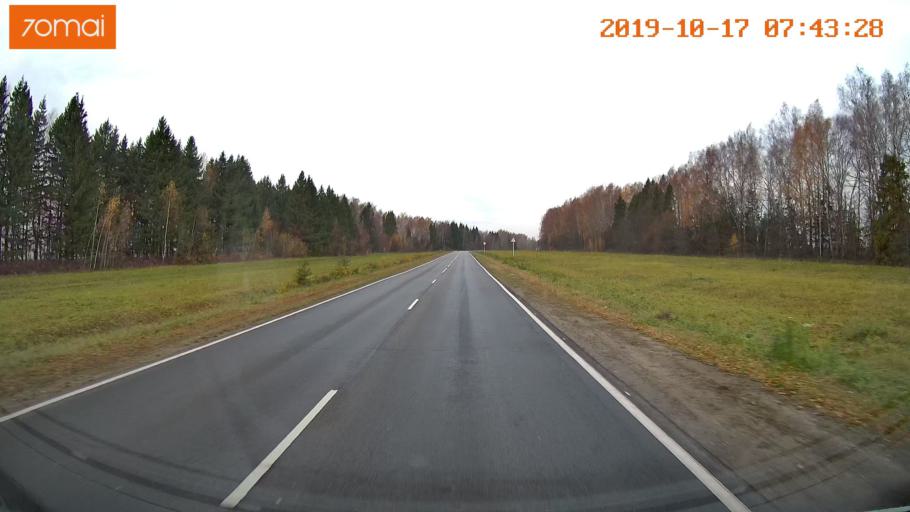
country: RU
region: Vladimir
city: Yur'yev-Pol'skiy
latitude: 56.4827
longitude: 39.7638
